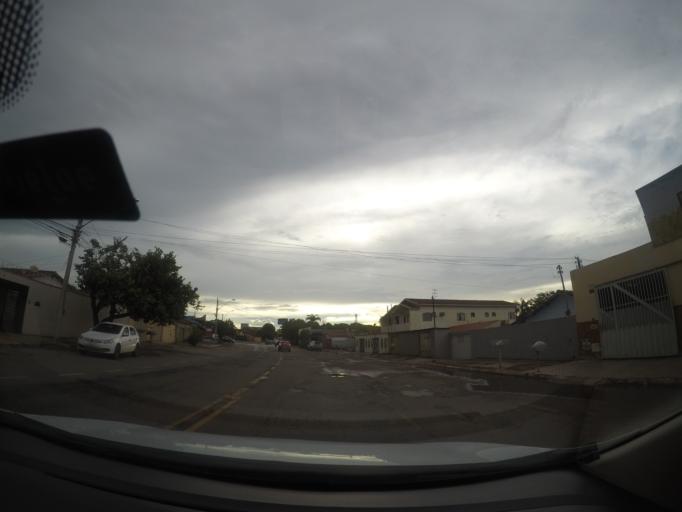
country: BR
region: Goias
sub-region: Goiania
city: Goiania
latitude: -16.6889
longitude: -49.3046
